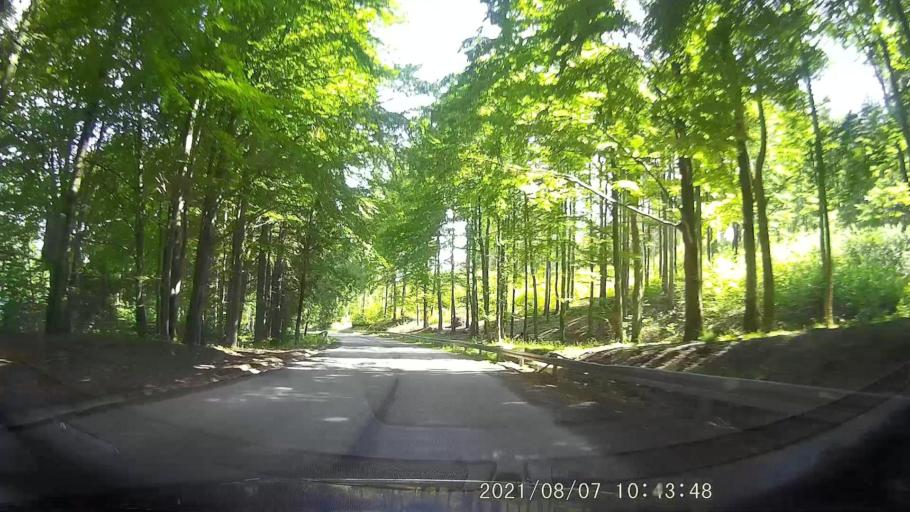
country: PL
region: Lower Silesian Voivodeship
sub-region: Powiat klodzki
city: Duszniki-Zdroj
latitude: 50.3270
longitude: 16.4010
